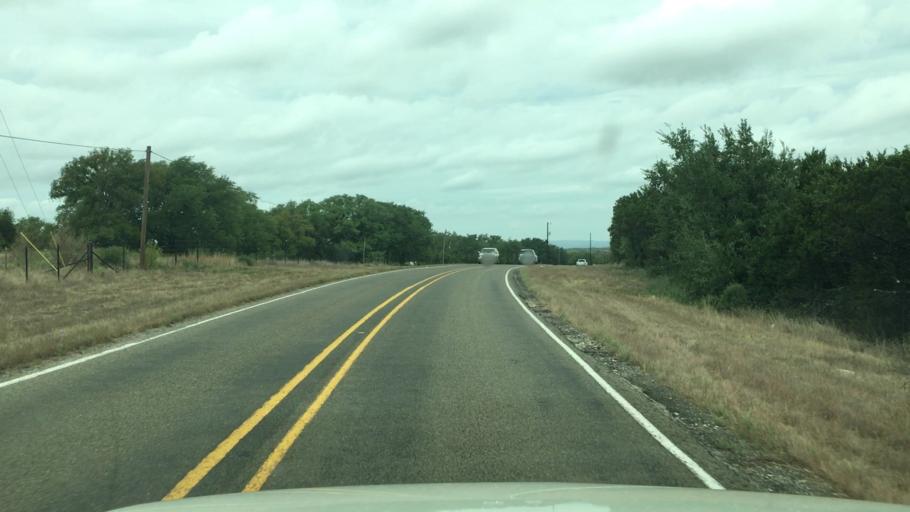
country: US
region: Texas
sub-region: Llano County
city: Horseshoe Bay
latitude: 30.4657
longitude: -98.4110
